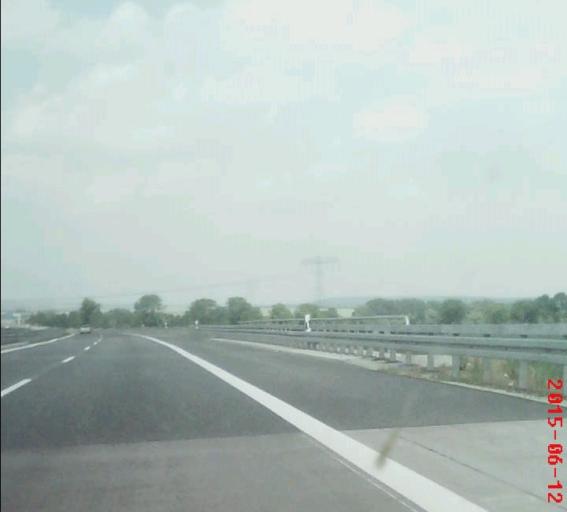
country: DE
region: Saxony-Anhalt
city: Oberroblingen
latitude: 51.4119
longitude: 11.3157
